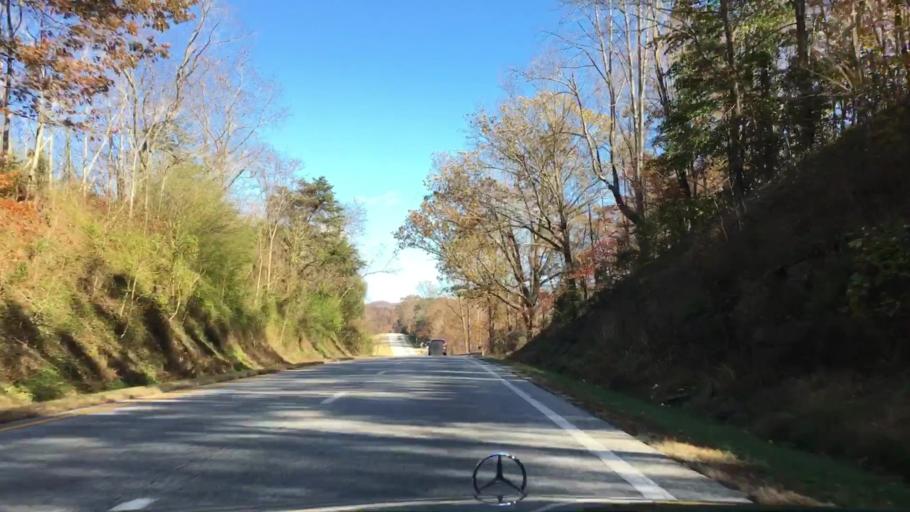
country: US
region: Virginia
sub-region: Nelson County
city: Nellysford
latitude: 37.8441
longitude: -78.7720
